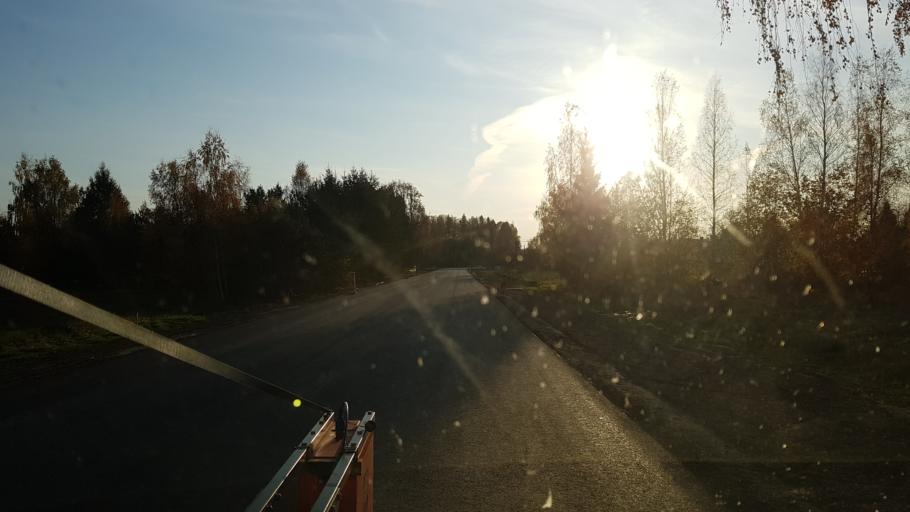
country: EE
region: Polvamaa
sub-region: Polva linn
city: Polva
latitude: 57.9460
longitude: 27.2153
